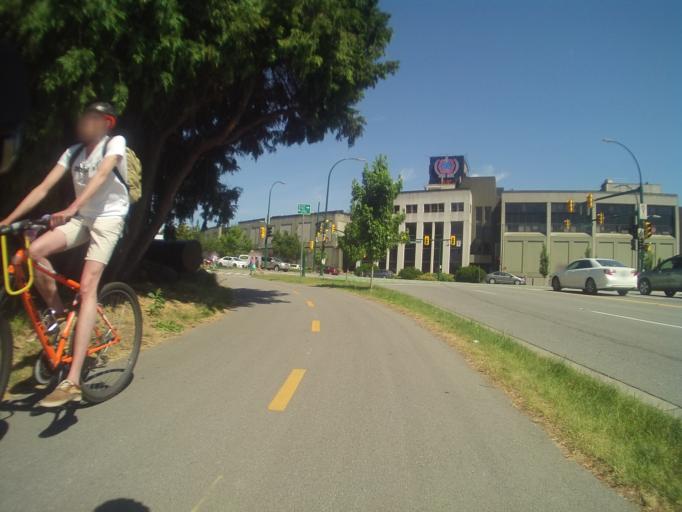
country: CA
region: British Columbia
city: West End
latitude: 49.2725
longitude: -123.1460
